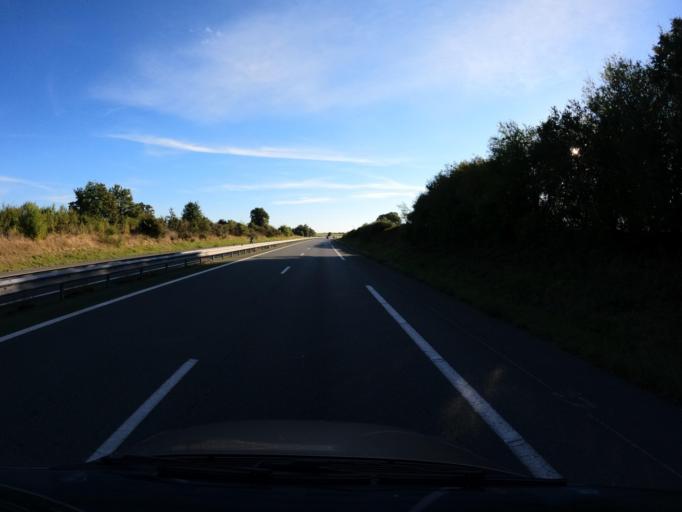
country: FR
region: Pays de la Loire
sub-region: Departement de Maine-et-Loire
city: Chemille-Melay
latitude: 47.1915
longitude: -0.7755
